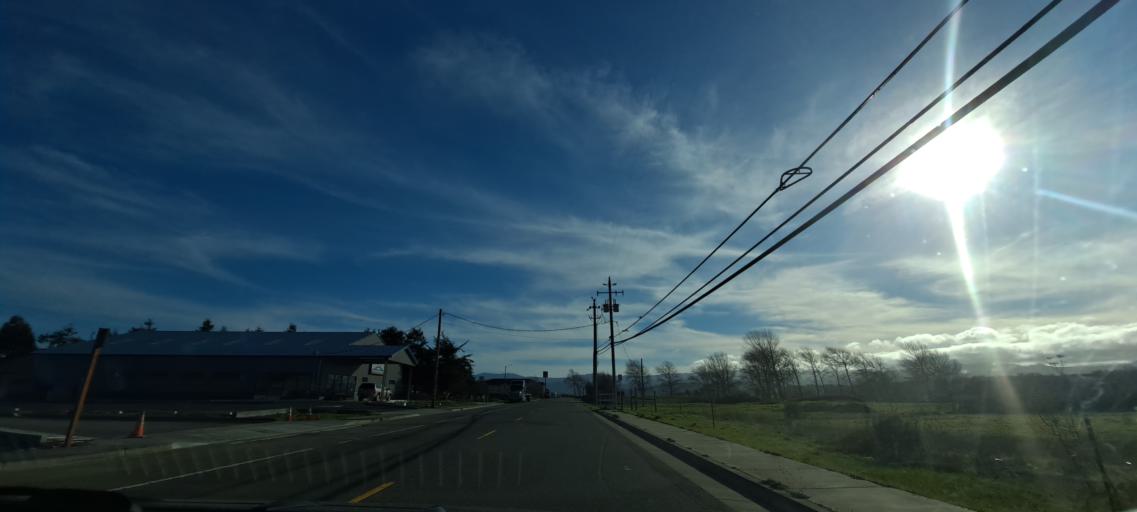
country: US
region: California
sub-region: Humboldt County
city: Fortuna
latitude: 40.5818
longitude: -124.1547
